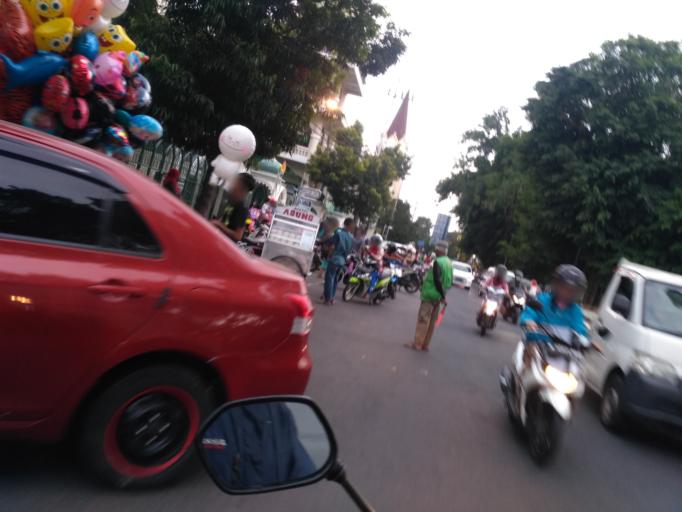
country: ID
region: East Java
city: Malang
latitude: -7.9828
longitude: 112.6301
